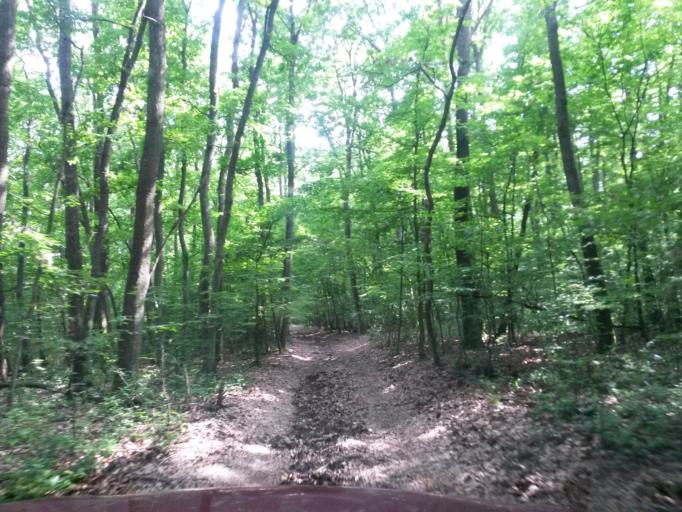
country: SK
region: Kosicky
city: Moldava nad Bodvou
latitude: 48.6258
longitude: 21.0996
